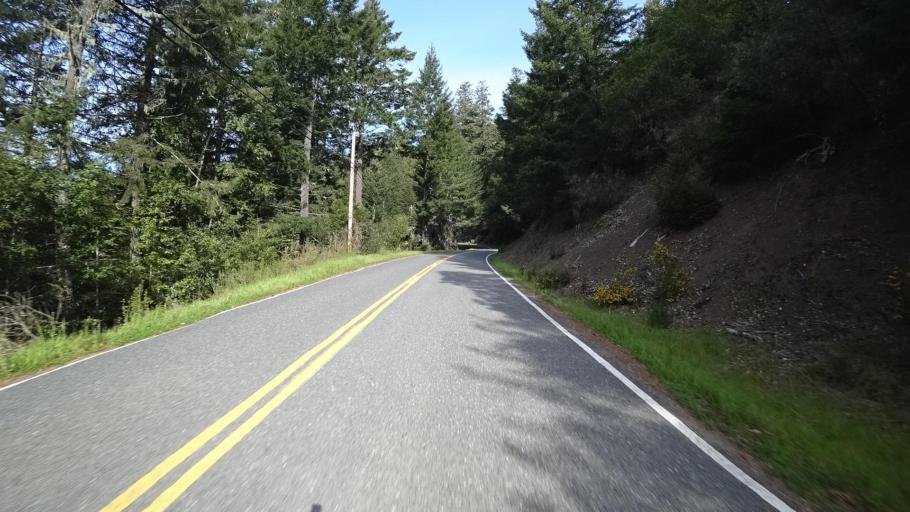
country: US
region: California
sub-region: Humboldt County
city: Bayside
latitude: 40.7477
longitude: -123.9684
